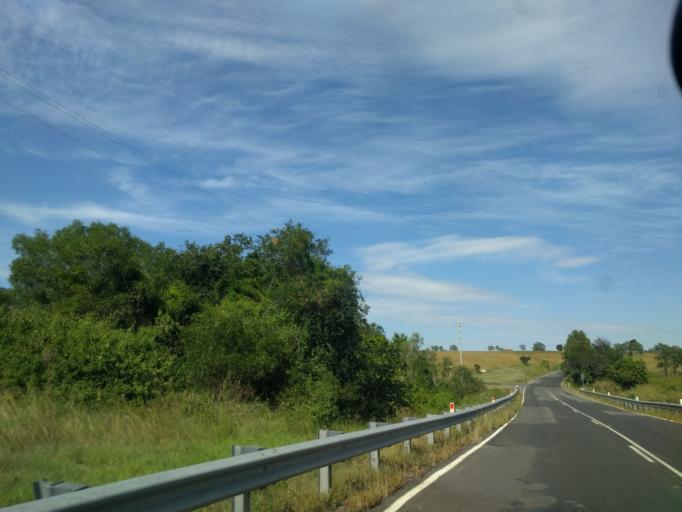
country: AU
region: Queensland
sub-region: Ipswich
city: Thagoona
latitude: -27.5927
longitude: 152.5517
